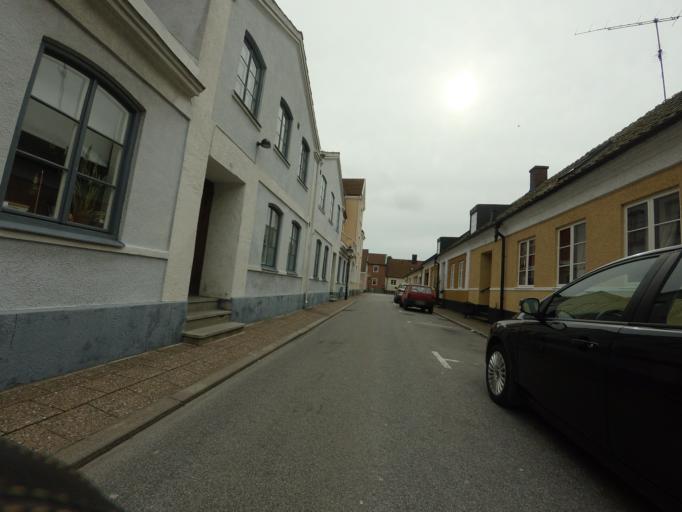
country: SE
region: Skane
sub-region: Ystads Kommun
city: Ystad
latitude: 55.4315
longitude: 13.8218
